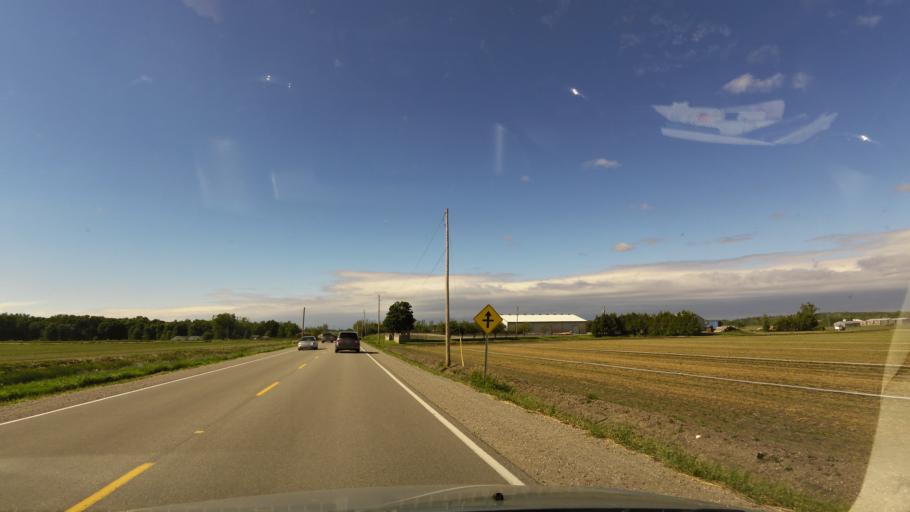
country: CA
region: Ontario
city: Innisfil
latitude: 44.2277
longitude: -79.6338
